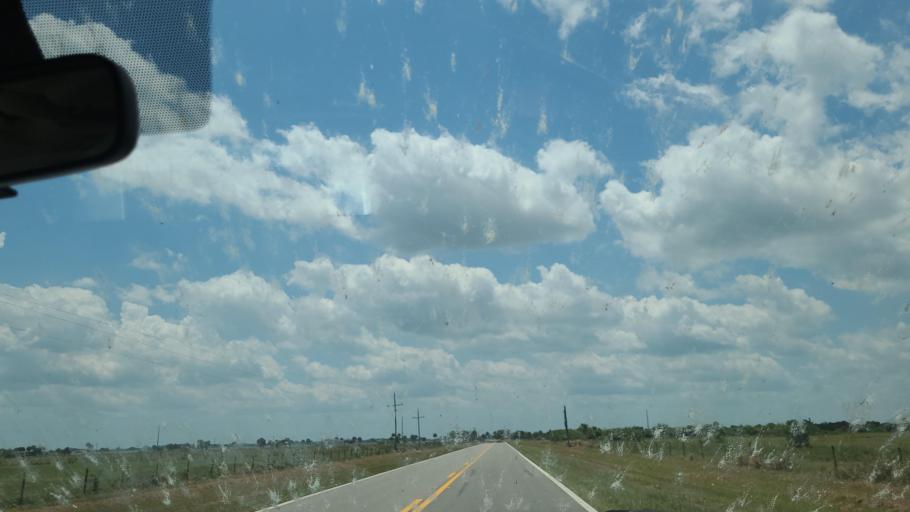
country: US
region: Florida
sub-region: Glades County
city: Buckhead Ridge
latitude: 27.2421
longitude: -81.0538
